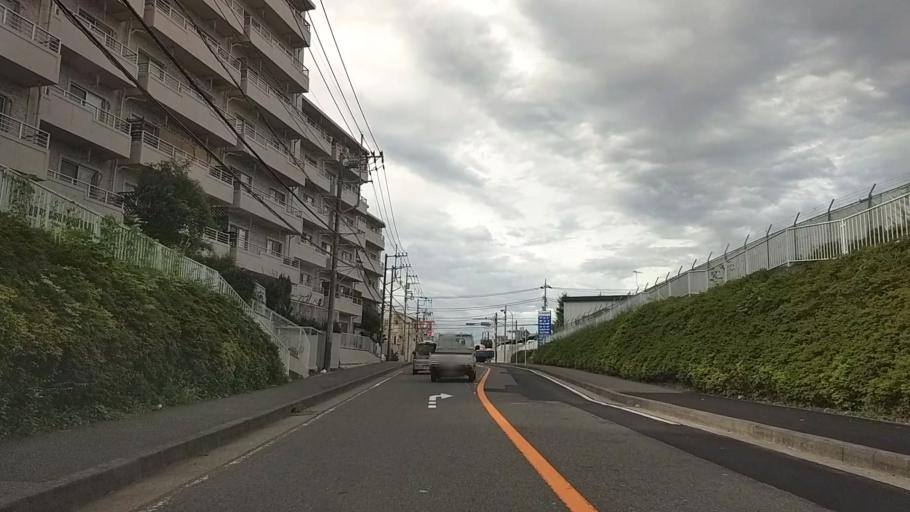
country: JP
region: Tokyo
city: Hachioji
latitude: 35.5770
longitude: 139.3412
